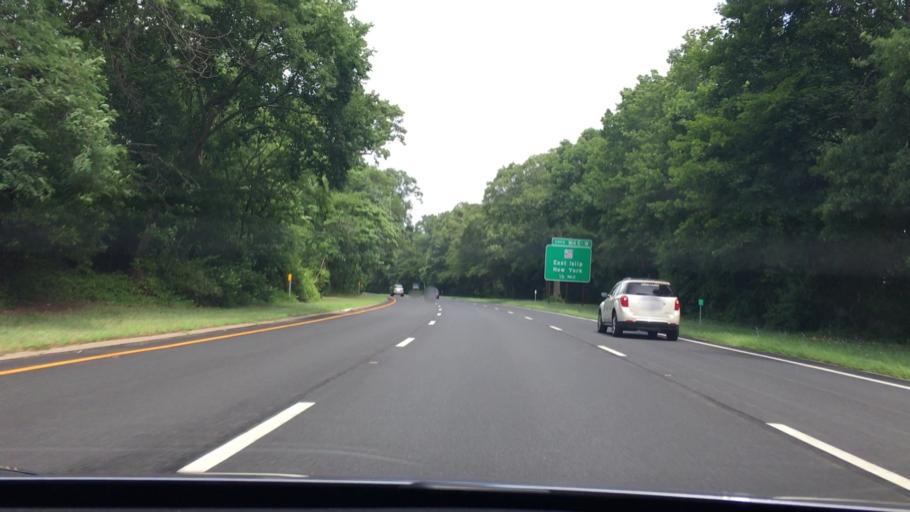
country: US
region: New York
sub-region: Nassau County
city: Wantagh
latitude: 40.6892
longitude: -73.5150
